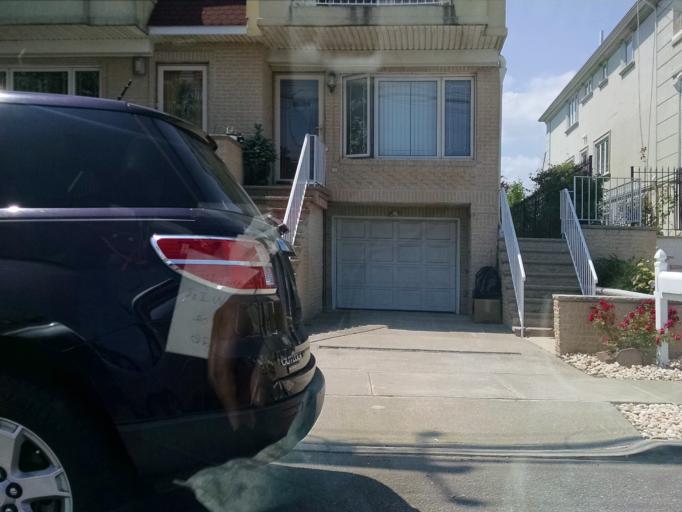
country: US
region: New York
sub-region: Richmond County
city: Staten Island
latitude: 40.5868
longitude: -74.0702
